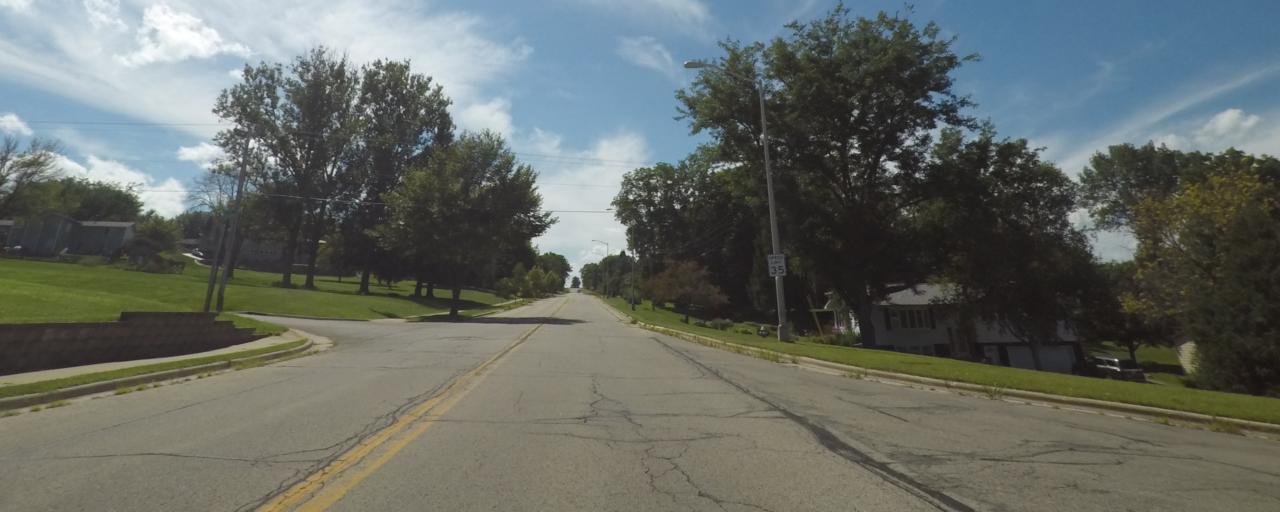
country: US
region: Wisconsin
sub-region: Green County
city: New Glarus
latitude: 42.8146
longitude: -89.6420
